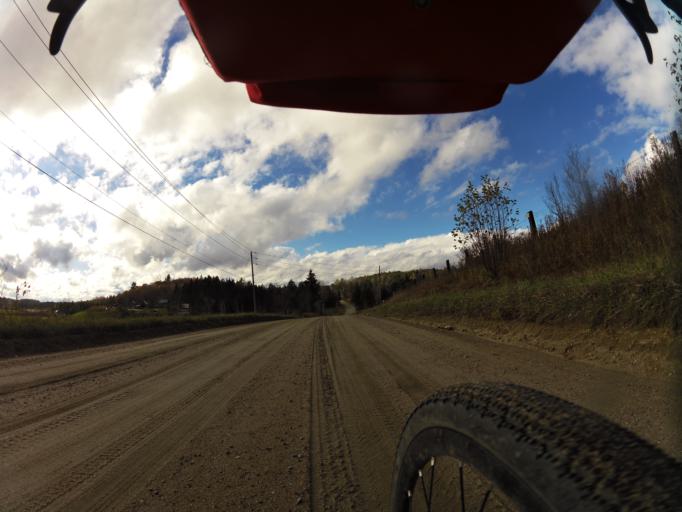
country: CA
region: Quebec
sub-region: Outaouais
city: Wakefield
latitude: 45.6980
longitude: -76.0790
